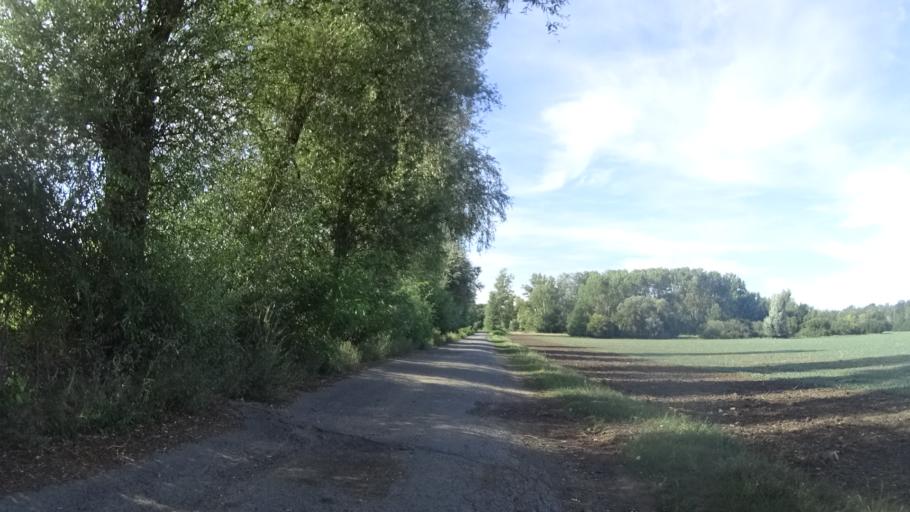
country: AT
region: Lower Austria
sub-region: Politischer Bezirk Ganserndorf
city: Drosing
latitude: 48.5933
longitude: 16.9502
